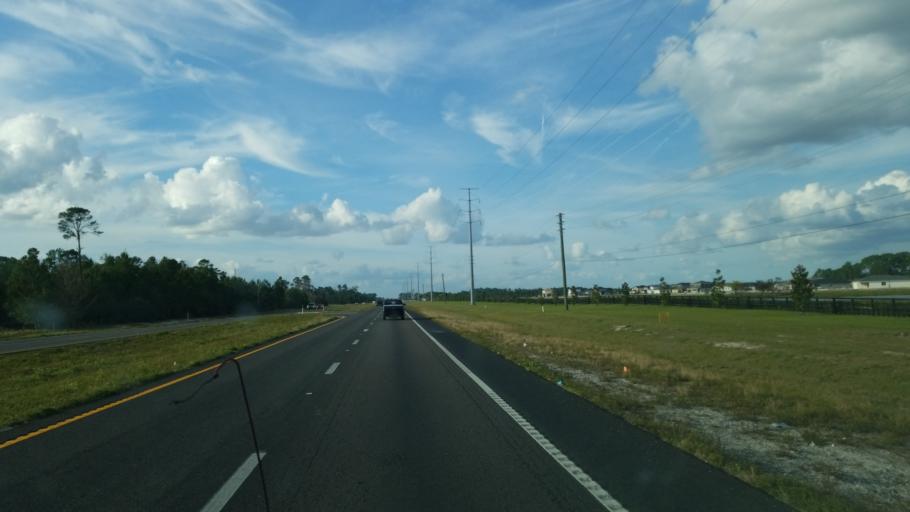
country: US
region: Florida
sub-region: Osceola County
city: Saint Cloud
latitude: 28.2052
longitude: -81.1697
